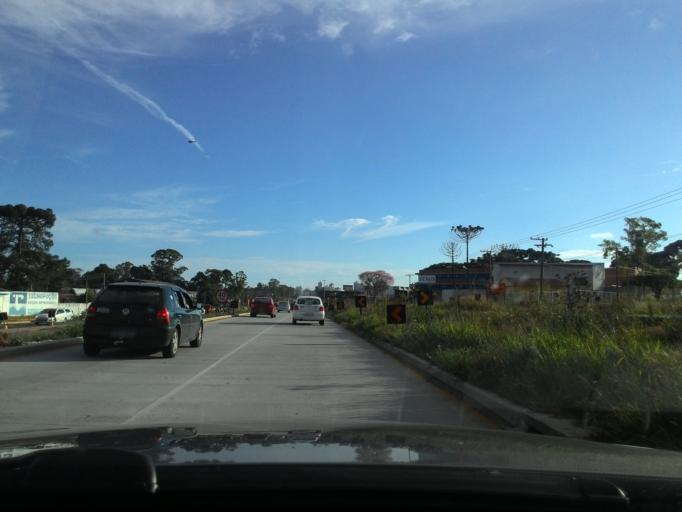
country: BR
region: Parana
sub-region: Pinhais
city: Pinhais
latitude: -25.4175
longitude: -49.2236
